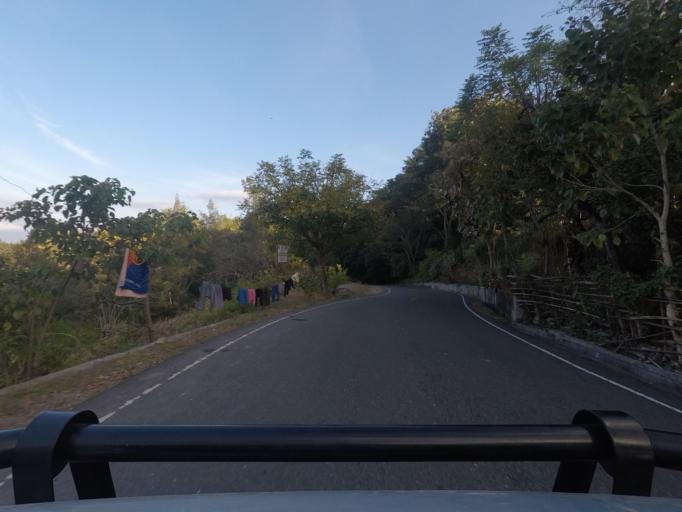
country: TL
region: Bobonaro
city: Maliana
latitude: -8.9535
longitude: 125.0746
